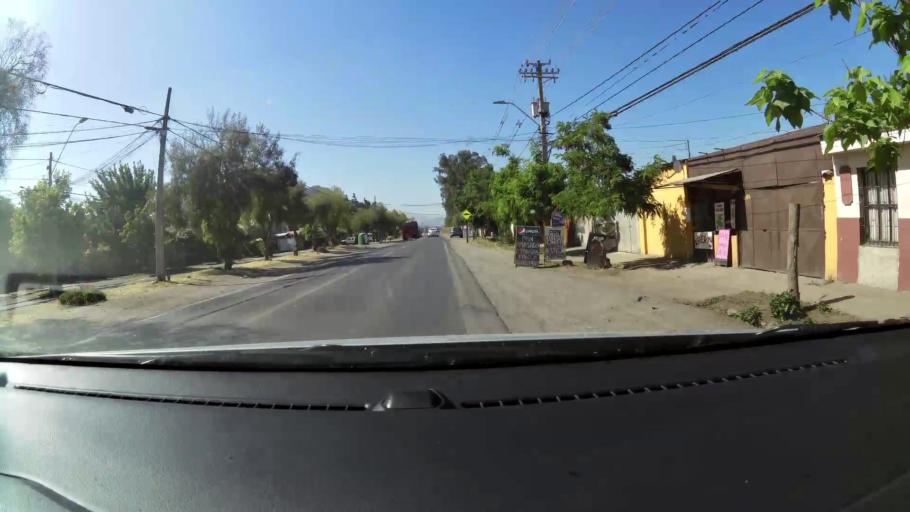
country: CL
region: Santiago Metropolitan
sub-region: Provincia de Maipo
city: San Bernardo
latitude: -33.6111
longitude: -70.6835
